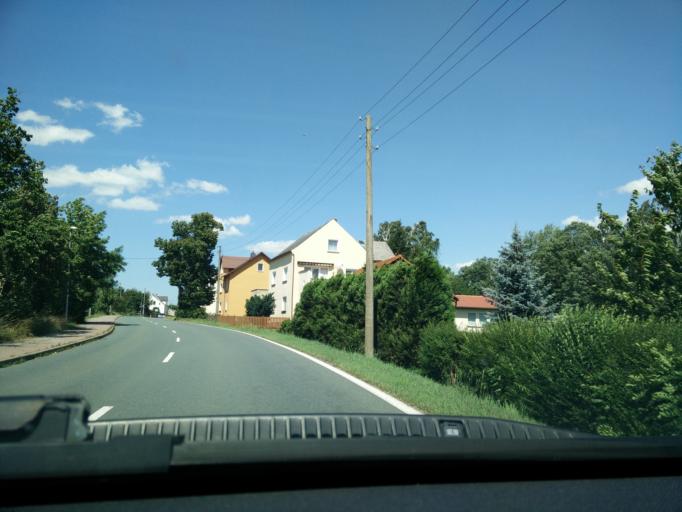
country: DE
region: Saxony
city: Narsdorf
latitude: 51.0042
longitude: 12.7084
